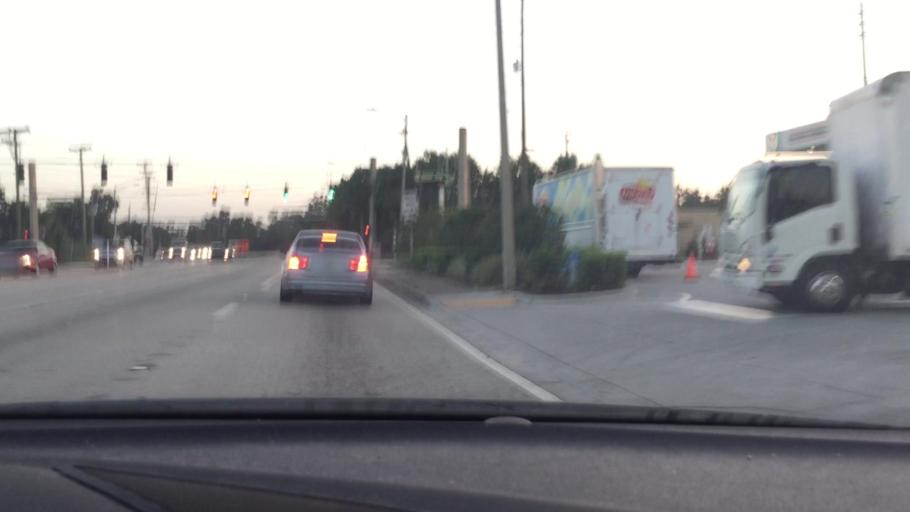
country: US
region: Florida
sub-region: Orange County
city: Fairview Shores
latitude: 28.5776
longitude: -81.4069
